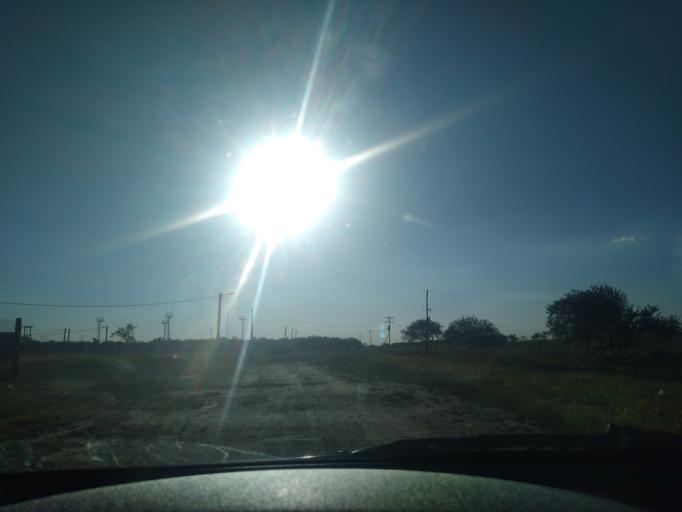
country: AR
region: Chaco
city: Resistencia
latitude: -27.4088
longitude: -58.9523
